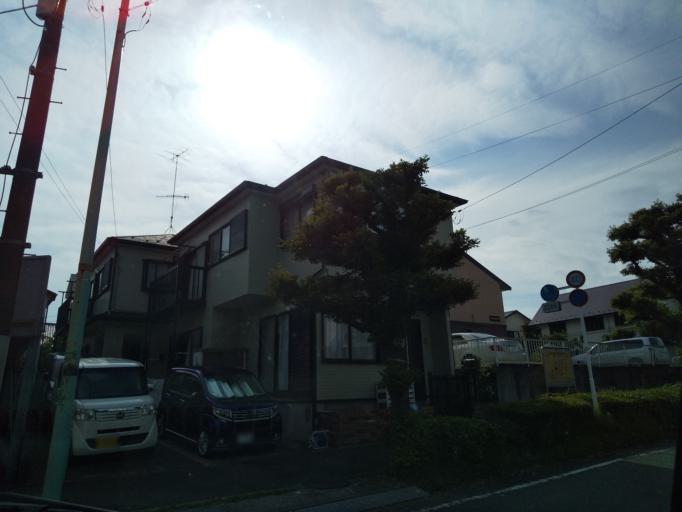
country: JP
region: Kanagawa
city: Zama
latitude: 35.4890
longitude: 139.3358
